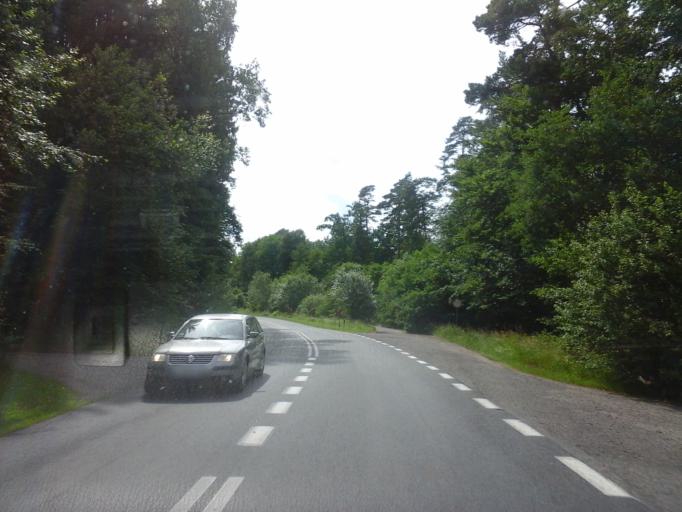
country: PL
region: West Pomeranian Voivodeship
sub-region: Powiat lobeski
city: Lobez
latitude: 53.5973
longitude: 15.6051
